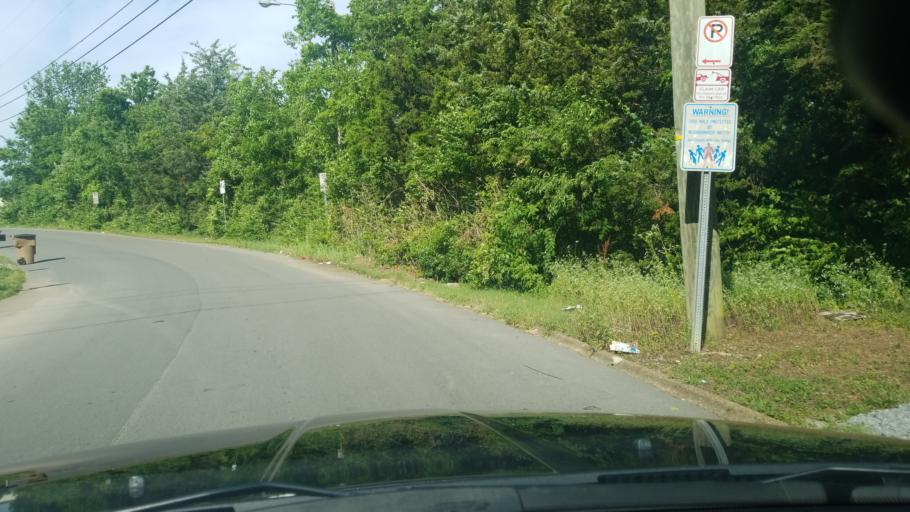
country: US
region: Tennessee
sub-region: Davidson County
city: Nashville
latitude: 36.2378
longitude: -86.7794
